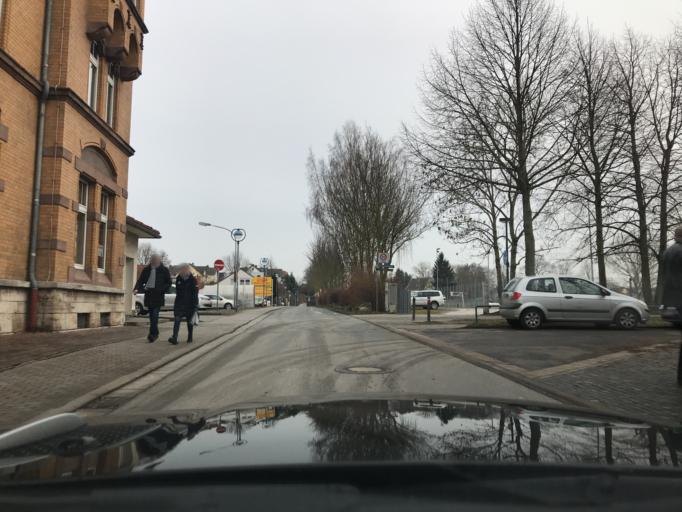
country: DE
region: Thuringia
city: Muehlhausen
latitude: 51.2037
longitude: 10.4401
